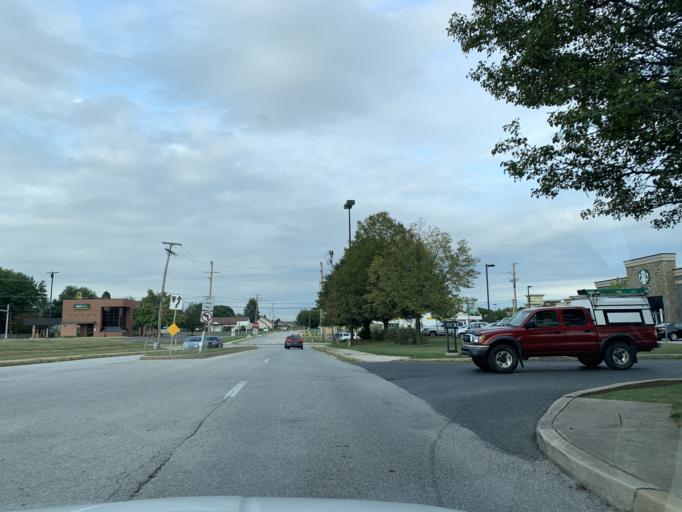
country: US
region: Pennsylvania
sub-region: York County
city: West York
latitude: 39.9751
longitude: -76.7676
